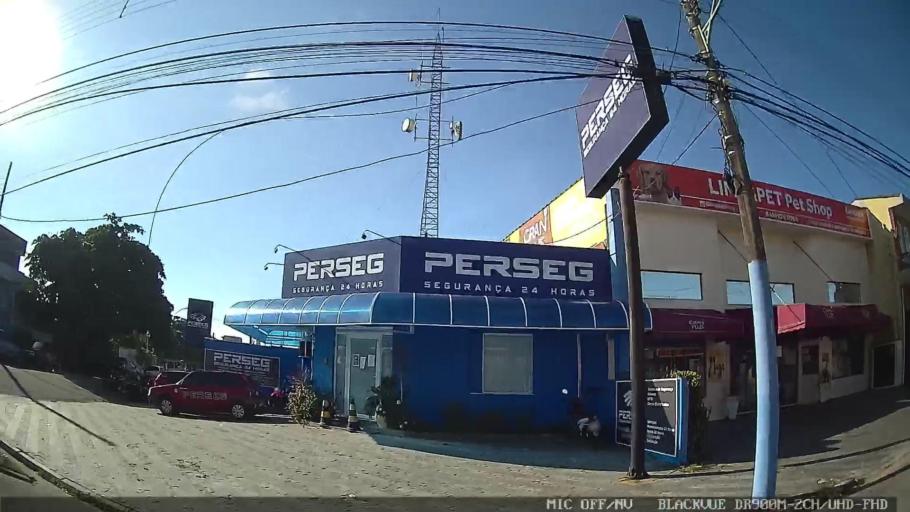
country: BR
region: Sao Paulo
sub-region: Peruibe
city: Peruibe
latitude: -24.2866
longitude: -46.9569
